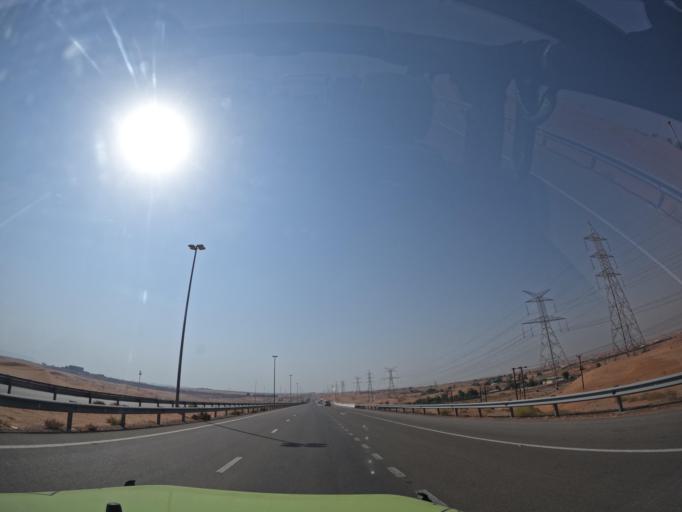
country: OM
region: Al Buraimi
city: Al Buraymi
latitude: 24.3459
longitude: 55.7393
